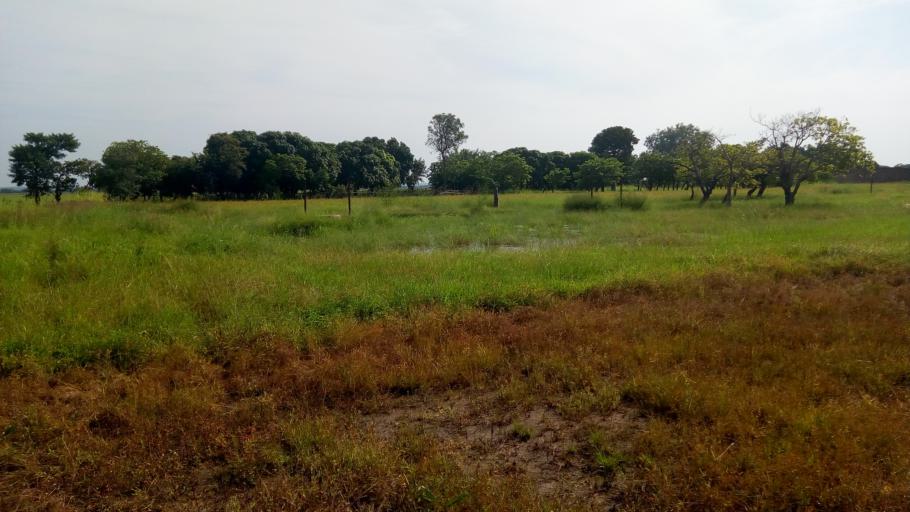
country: ML
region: Koulikoro
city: Kangaba
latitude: 11.6788
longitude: -8.7099
